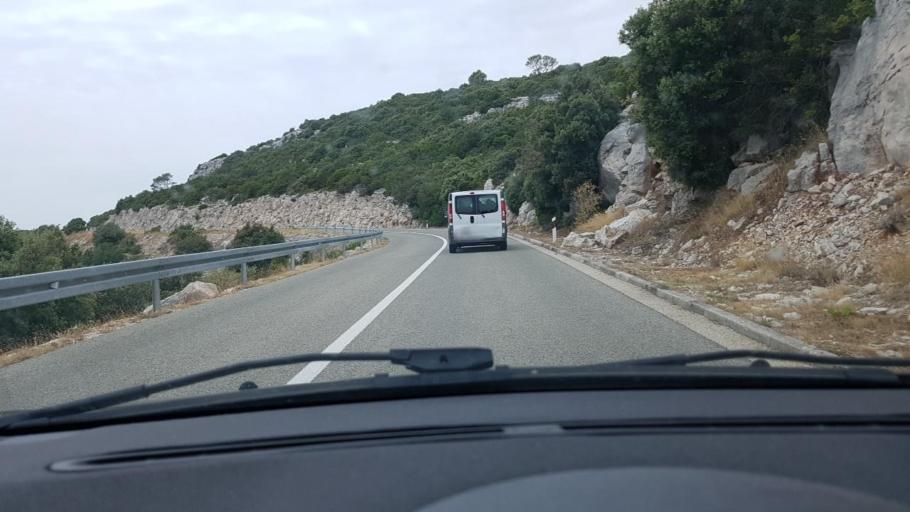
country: HR
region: Dubrovacko-Neretvanska
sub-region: Grad Korcula
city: Zrnovo
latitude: 42.9385
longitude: 17.0135
